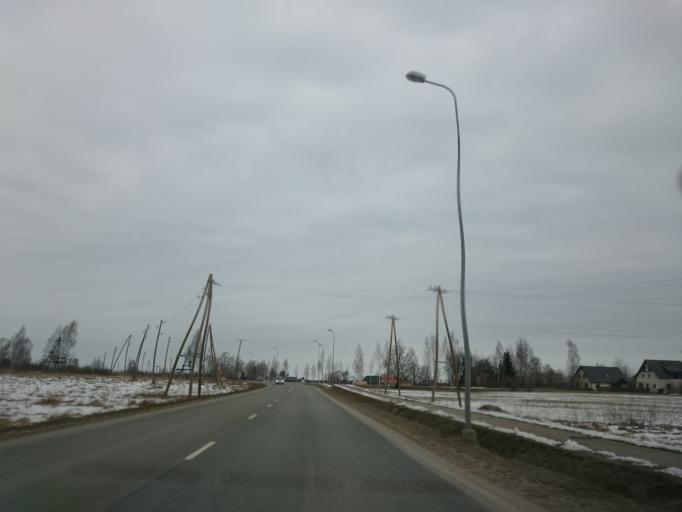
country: LV
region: Cesu Rajons
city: Cesis
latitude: 57.2998
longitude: 25.2455
